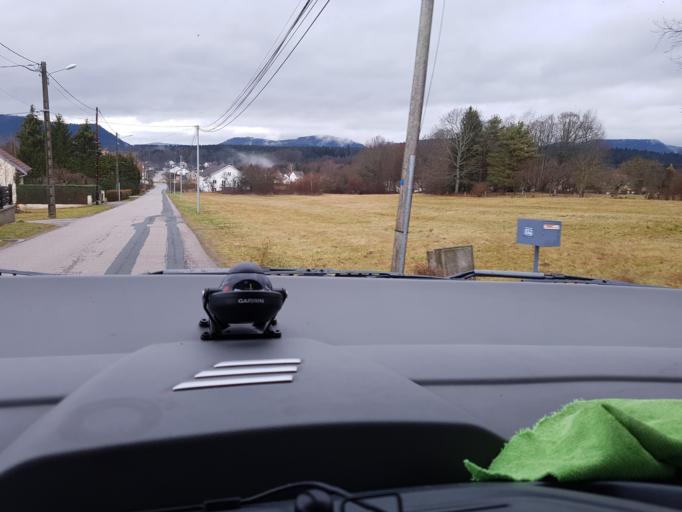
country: FR
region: Lorraine
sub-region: Departement des Vosges
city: Saint-Michel-sur-Meurthe
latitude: 48.3421
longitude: 6.8939
